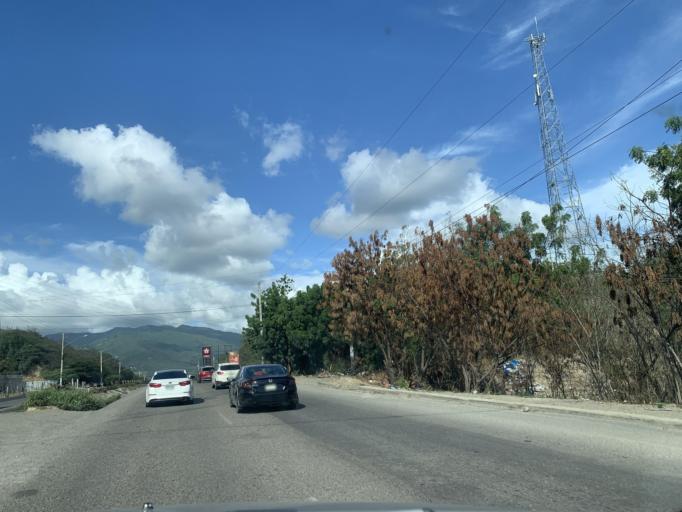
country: DO
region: Santiago
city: Villa Gonzalez
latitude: 19.5506
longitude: -70.8302
